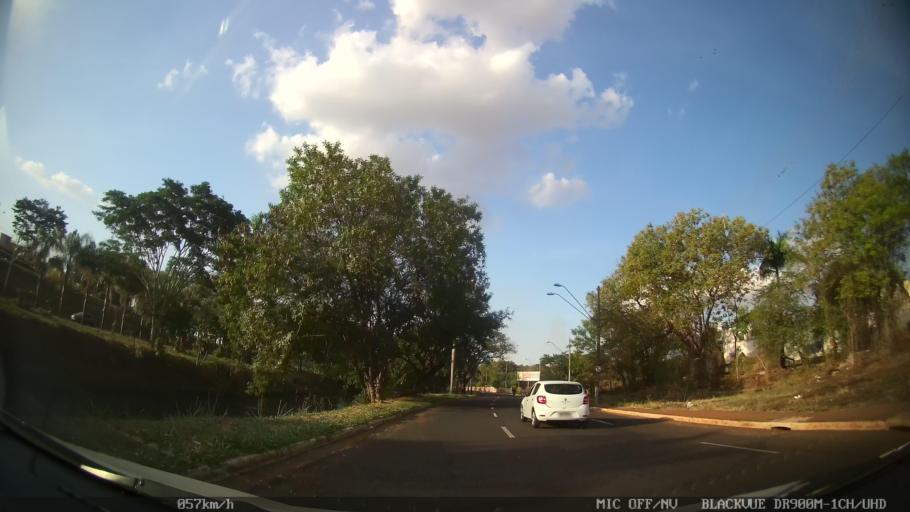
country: BR
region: Sao Paulo
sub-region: Ribeirao Preto
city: Ribeirao Preto
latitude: -21.1600
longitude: -47.8132
